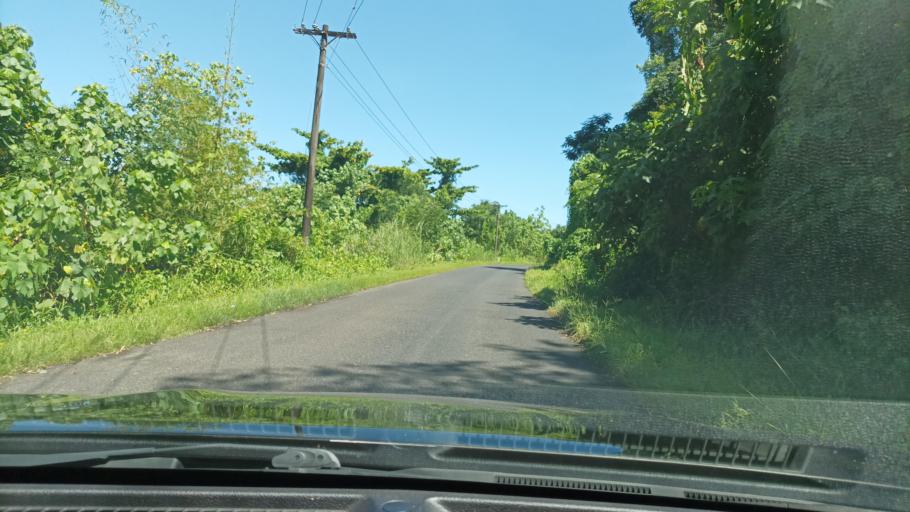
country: FM
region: Pohnpei
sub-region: Madolenihm Municipality
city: Madolenihm Municipality Government
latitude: 6.8623
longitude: 158.2934
